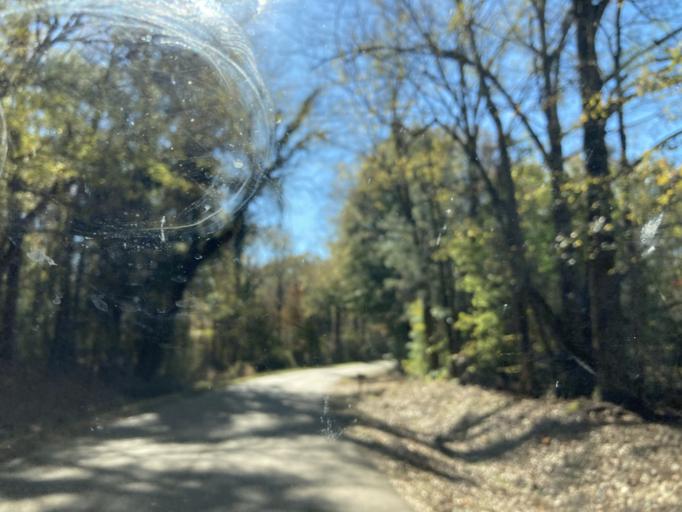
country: US
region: Mississippi
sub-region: Hinds County
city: Lynchburg
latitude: 32.5798
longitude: -90.5696
